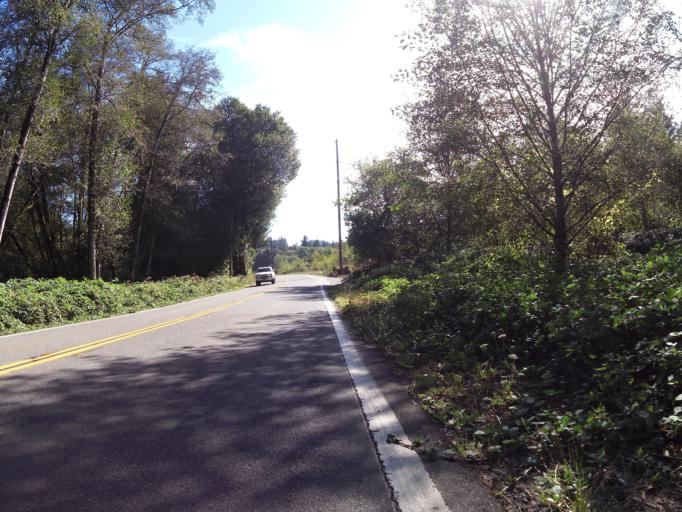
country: US
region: California
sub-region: Del Norte County
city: Bertsch-Oceanview
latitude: 41.8629
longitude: -124.1177
